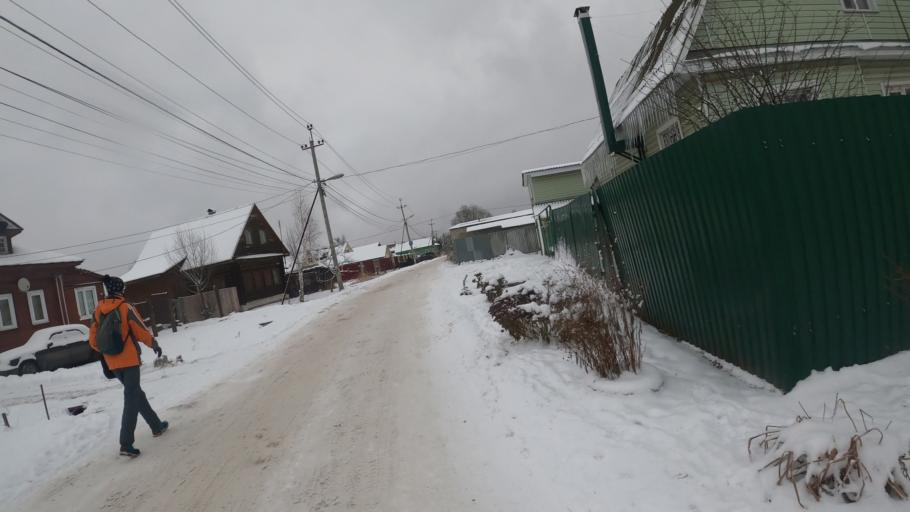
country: RU
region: Jaroslavl
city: Pereslavl'-Zalesskiy
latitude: 56.7328
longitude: 38.8364
